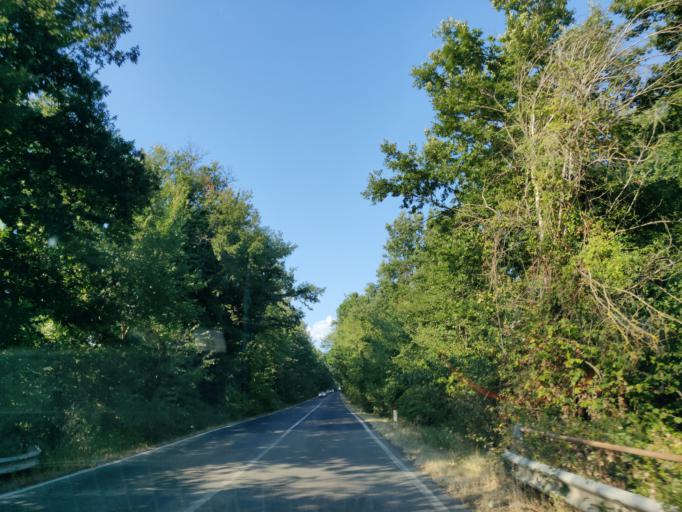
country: IT
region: Latium
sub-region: Provincia di Viterbo
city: Latera
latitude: 42.5966
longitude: 11.8389
